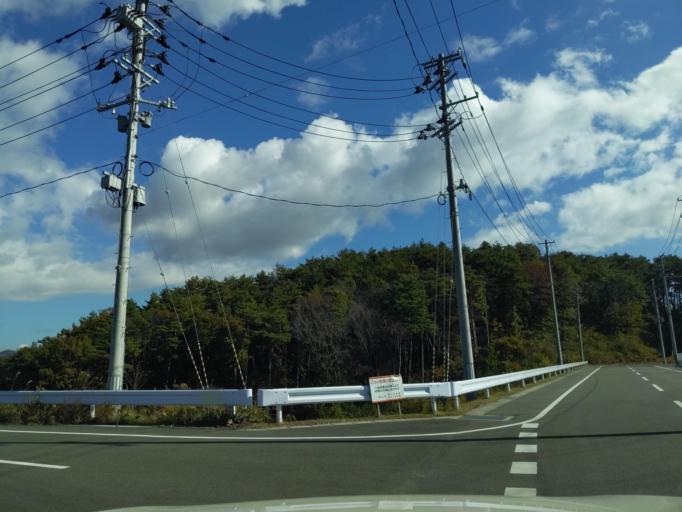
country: JP
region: Fukushima
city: Koriyama
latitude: 37.4642
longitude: 140.3034
